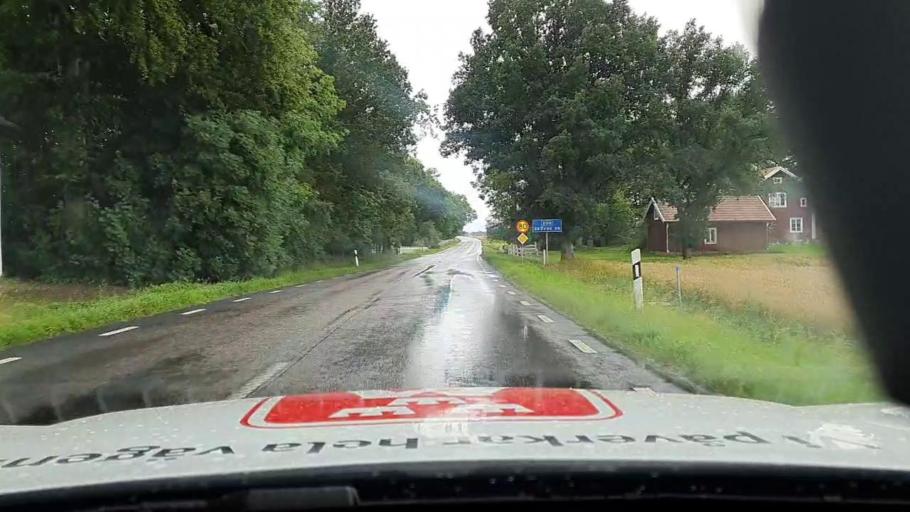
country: SE
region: Vaestra Goetaland
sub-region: Toreboda Kommun
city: Toereboda
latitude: 58.6070
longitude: 14.0098
